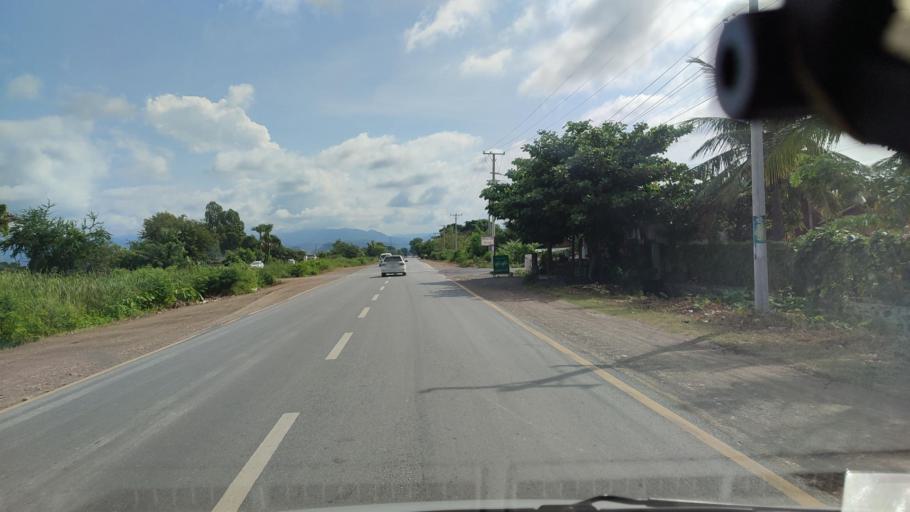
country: MM
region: Mandalay
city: Mandalay
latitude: 21.8661
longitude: 96.1624
